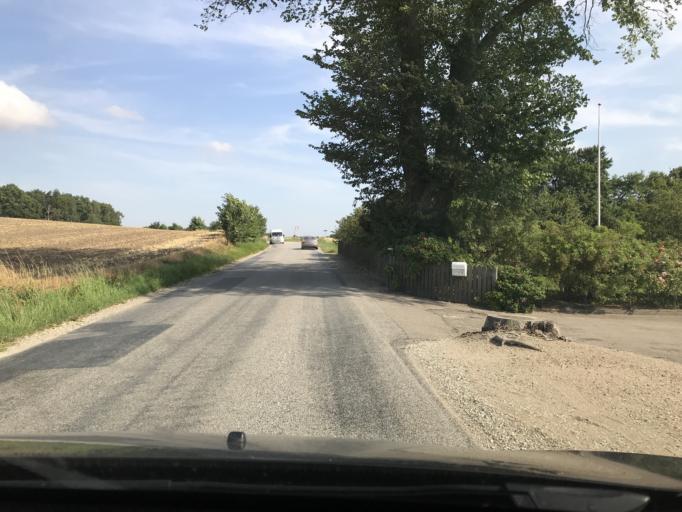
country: DK
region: Central Jutland
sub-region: Norddjurs Kommune
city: Allingabro
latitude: 56.4505
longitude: 10.3099
